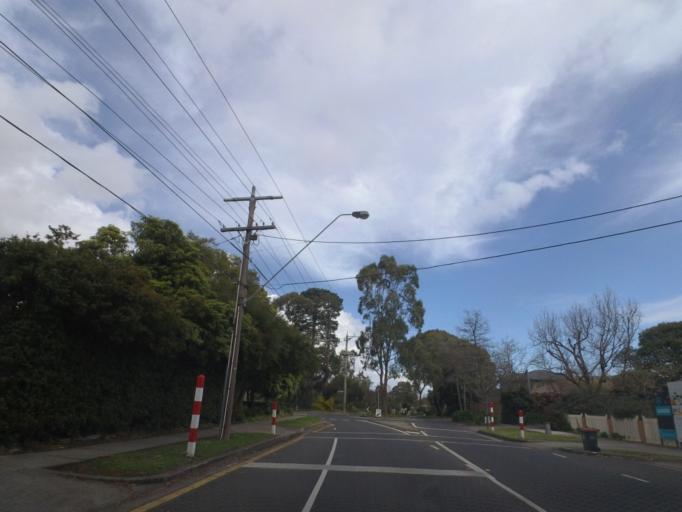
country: AU
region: Victoria
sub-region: Whitehorse
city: Vermont
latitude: -37.8386
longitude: 145.1908
